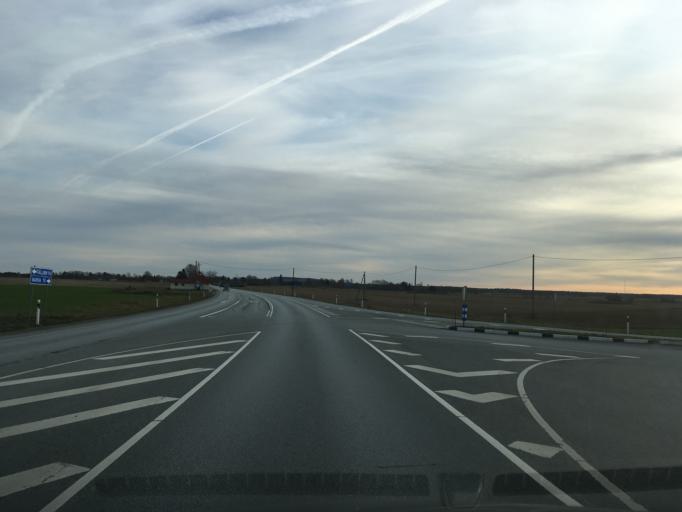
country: EE
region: Ida-Virumaa
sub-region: Puessi linn
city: Pussi
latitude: 59.4034
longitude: 27.0734
